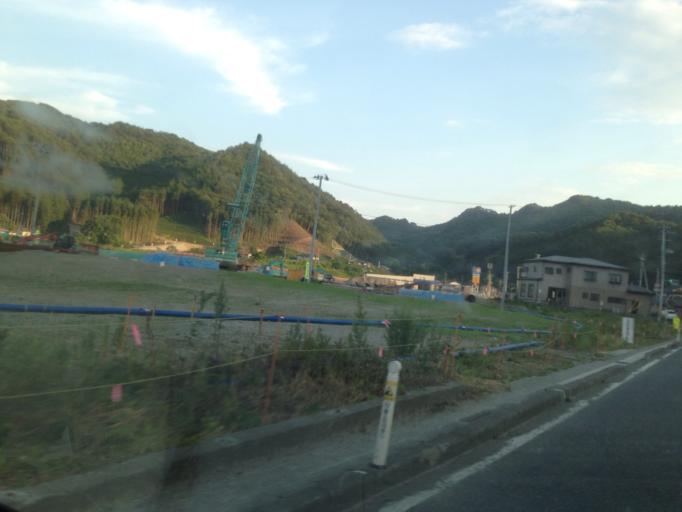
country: JP
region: Iwate
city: Otsuchi
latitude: 39.3245
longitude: 141.8851
